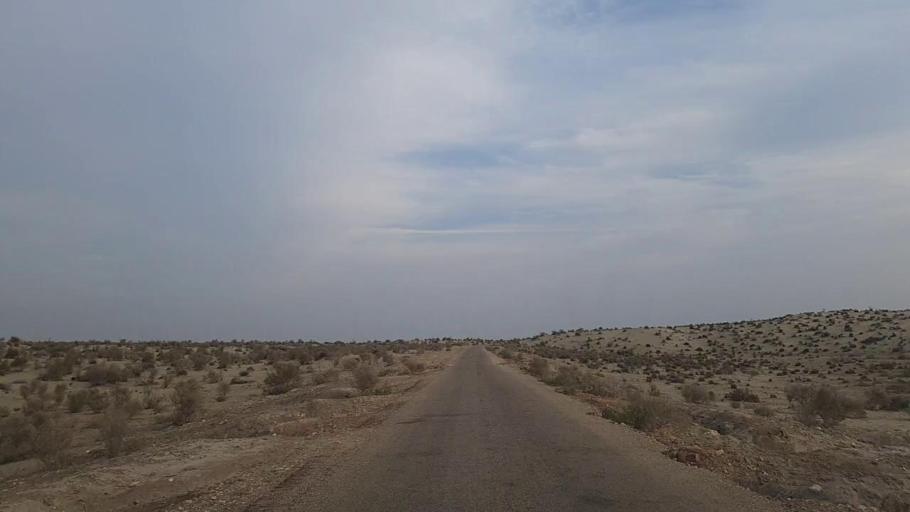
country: PK
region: Sindh
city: Daur
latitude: 26.5049
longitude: 68.5164
